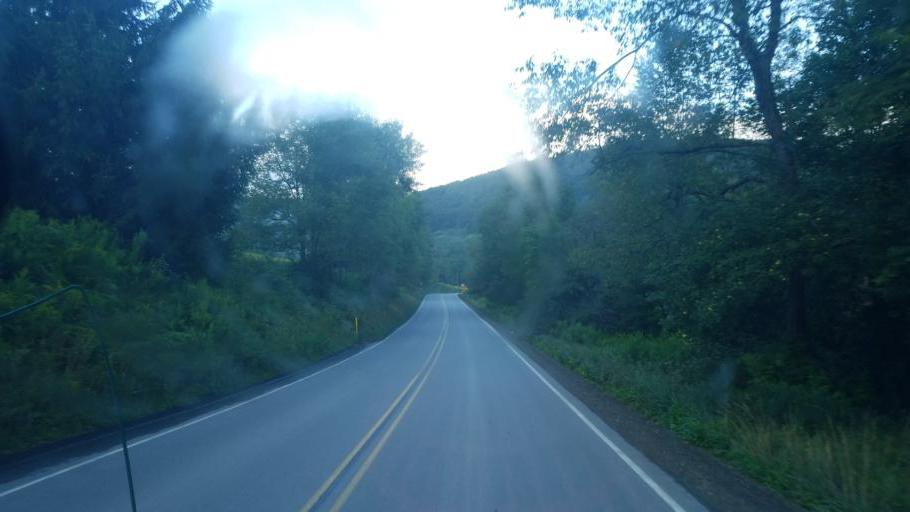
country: US
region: Pennsylvania
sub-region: Potter County
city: Galeton
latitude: 41.8384
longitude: -77.7918
